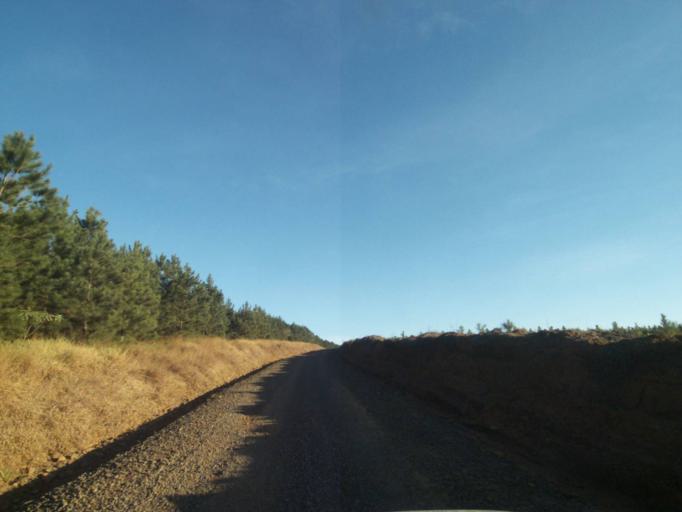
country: BR
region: Parana
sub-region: Telemaco Borba
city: Telemaco Borba
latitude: -24.4514
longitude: -50.5994
